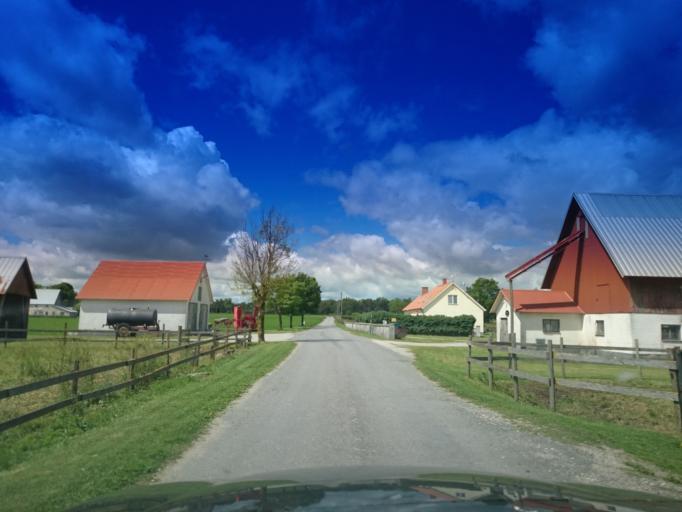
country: SE
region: Gotland
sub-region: Gotland
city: Hemse
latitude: 57.3425
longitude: 18.6383
